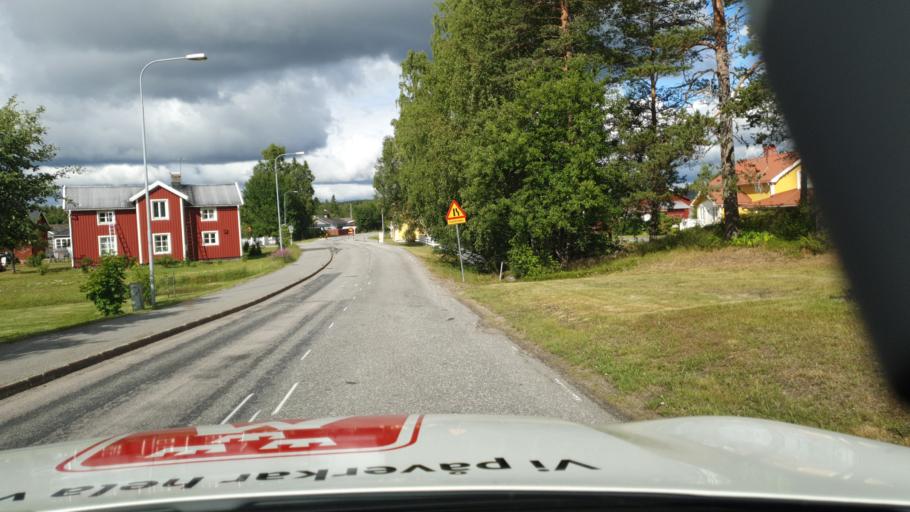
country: SE
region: Vaesterbotten
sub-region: Umea Kommun
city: Hoernefors
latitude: 63.6805
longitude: 20.0101
